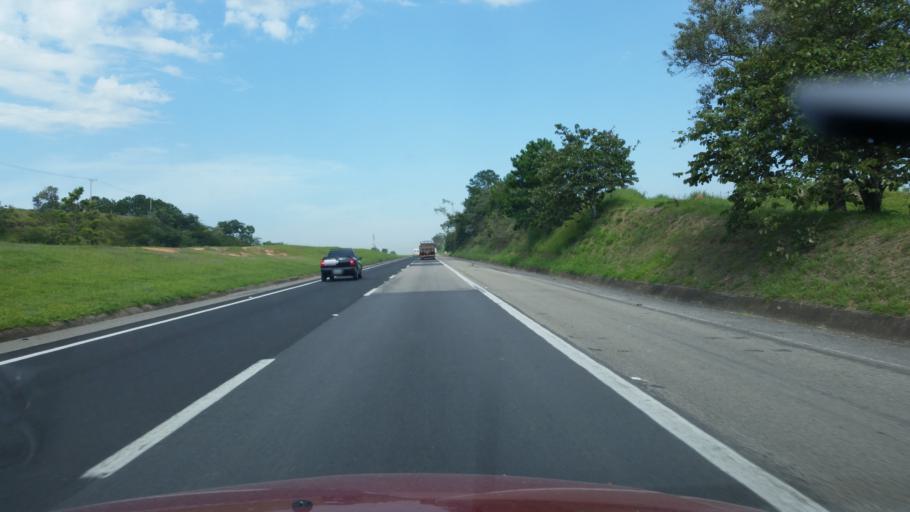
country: BR
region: Sao Paulo
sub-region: Sorocaba
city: Sorocaba
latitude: -23.3775
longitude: -47.4134
